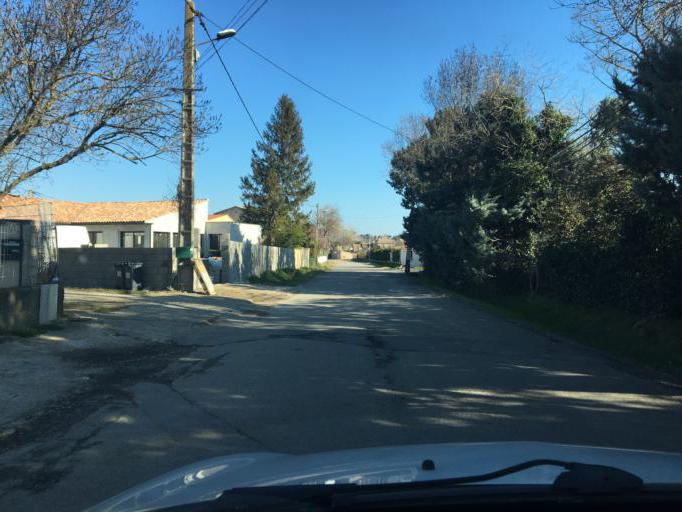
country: FR
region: Languedoc-Roussillon
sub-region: Departement du Gard
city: Les Angles
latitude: 43.9460
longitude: 4.7788
